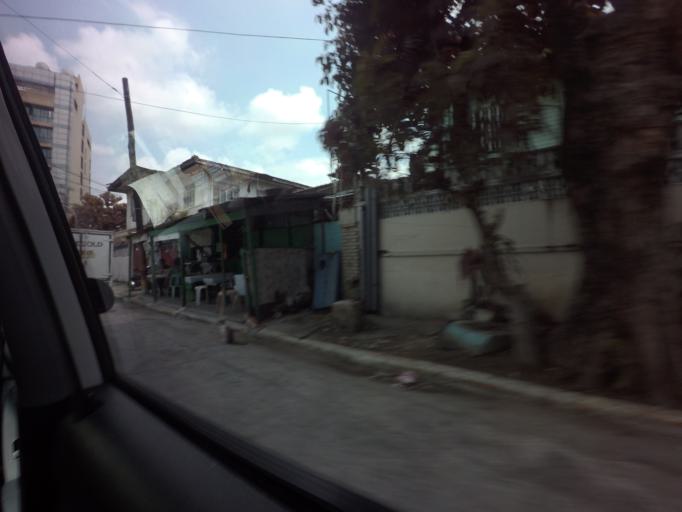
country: PH
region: Metro Manila
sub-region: San Juan
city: San Juan
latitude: 14.5927
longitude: 121.0199
